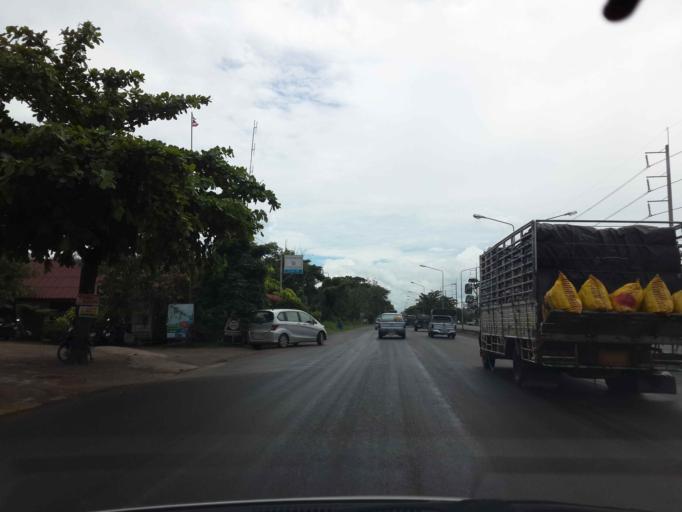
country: TH
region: Ratchaburi
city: Ratchaburi
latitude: 13.4564
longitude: 99.7999
